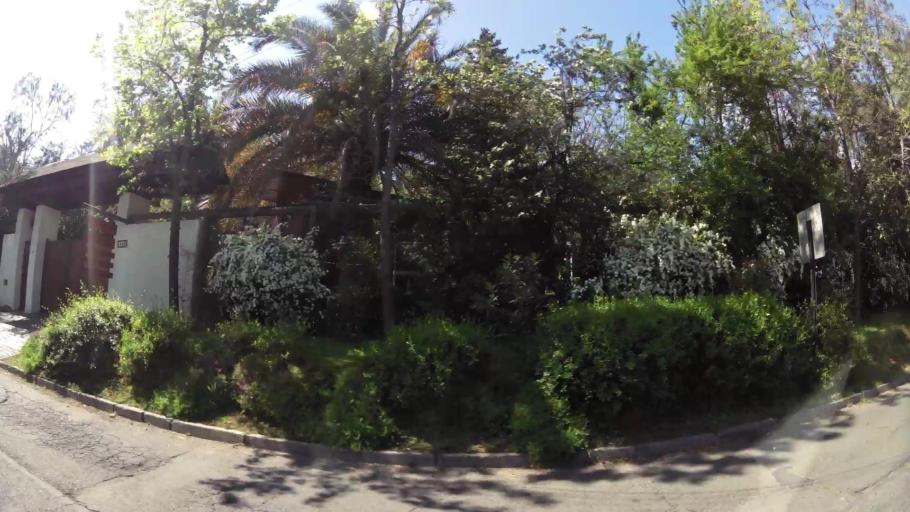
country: CL
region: Santiago Metropolitan
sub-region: Provincia de Santiago
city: Villa Presidente Frei, Nunoa, Santiago, Chile
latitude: -33.4467
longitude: -70.5230
